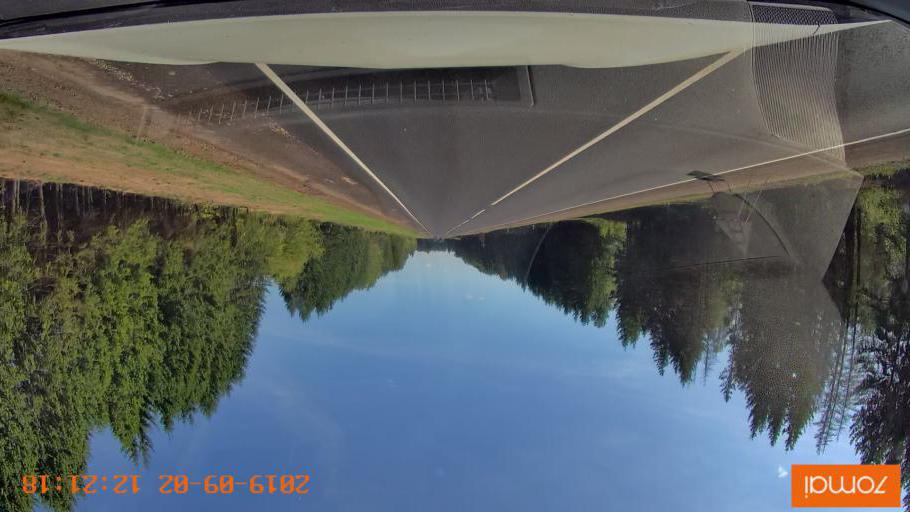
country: RU
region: Smolensk
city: Oster
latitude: 53.8884
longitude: 32.6583
